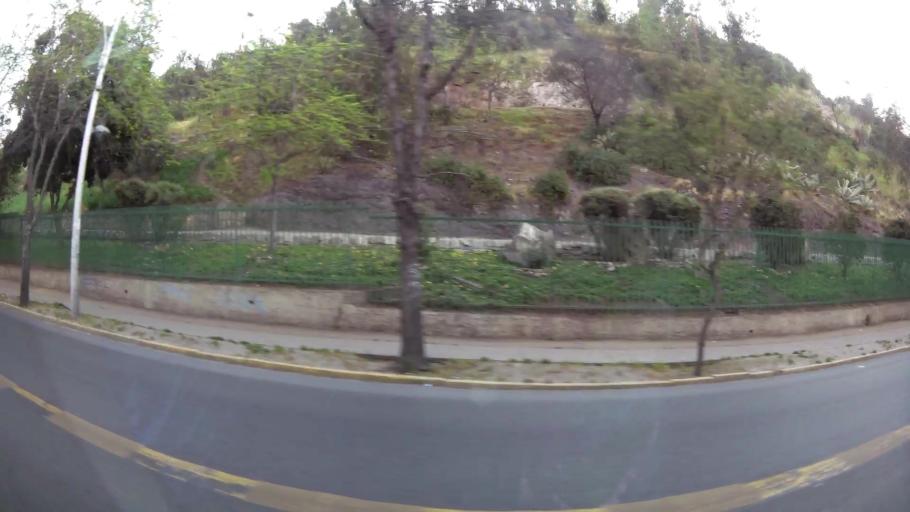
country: CL
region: Santiago Metropolitan
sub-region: Provincia de Santiago
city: Santiago
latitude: -33.4197
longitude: -70.6442
